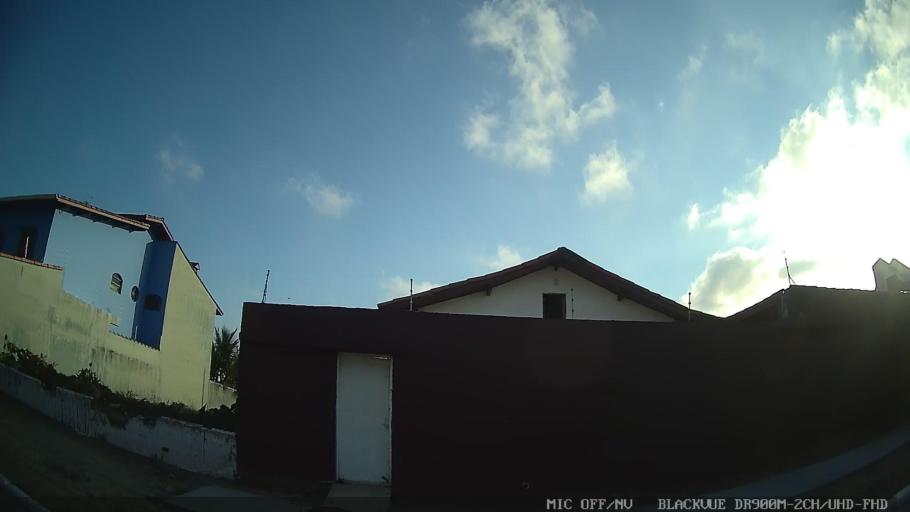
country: BR
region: Sao Paulo
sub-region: Peruibe
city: Peruibe
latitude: -24.2978
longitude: -46.9665
